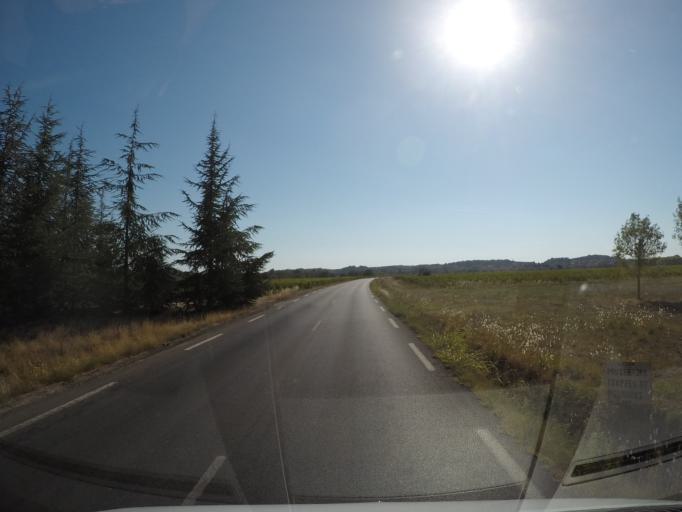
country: FR
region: Languedoc-Roussillon
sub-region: Departement du Gard
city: Lezan
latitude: 44.0238
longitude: 4.0359
